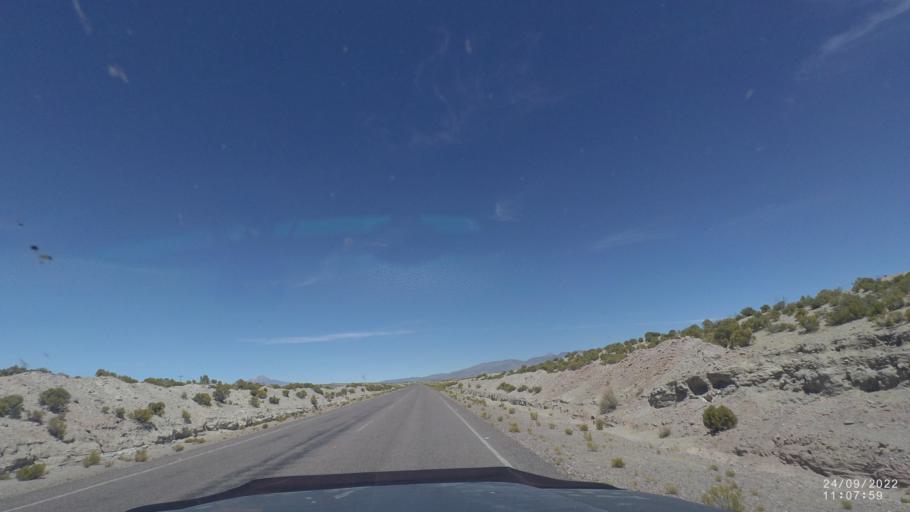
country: BO
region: Oruro
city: Challapata
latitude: -19.4810
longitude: -67.4370
